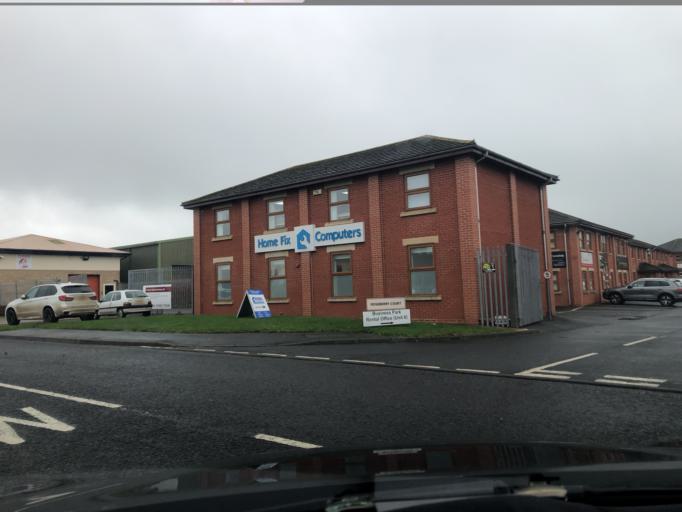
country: GB
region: England
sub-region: North Yorkshire
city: Stokesley
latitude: 54.4616
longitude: -1.1788
